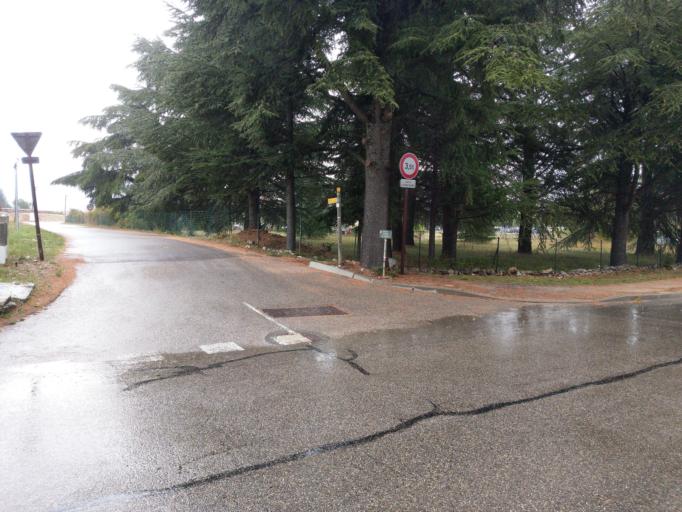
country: FR
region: Provence-Alpes-Cote d'Azur
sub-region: Departement du Vaucluse
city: Sault
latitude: 44.0954
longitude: 5.4118
